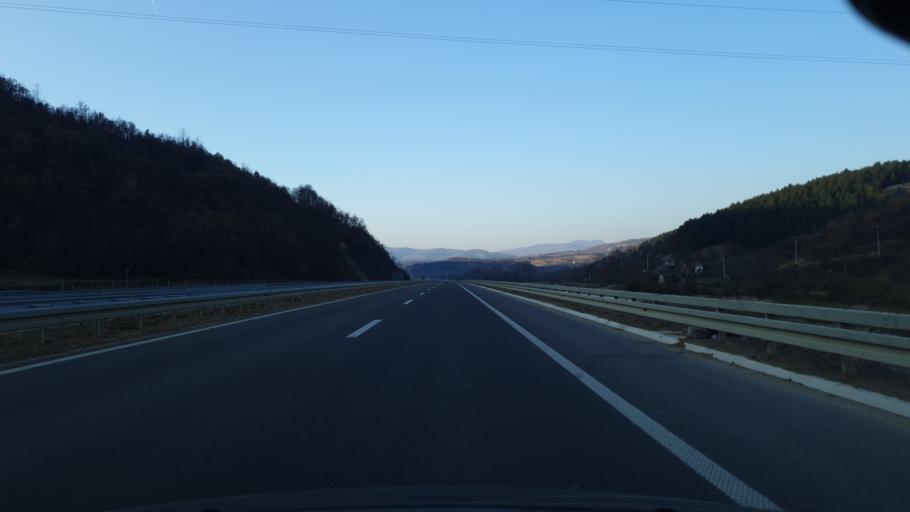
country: RS
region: Central Serbia
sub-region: Pirotski Okrug
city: Pirot
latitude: 43.1962
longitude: 22.5612
